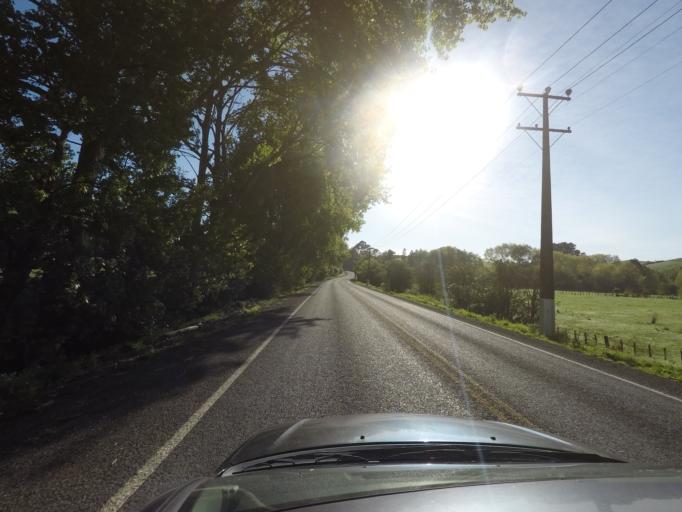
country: NZ
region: Auckland
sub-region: Auckland
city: Red Hill
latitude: -36.9968
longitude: 174.9793
